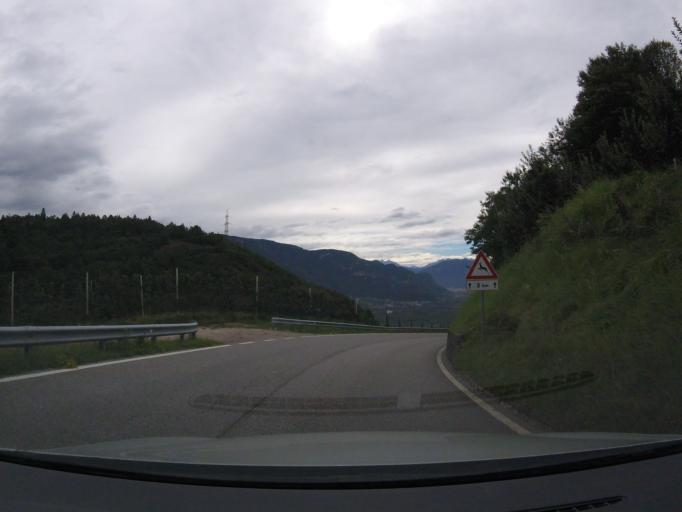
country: IT
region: Trentino-Alto Adige
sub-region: Bolzano
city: Tesimo
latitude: 46.5523
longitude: 11.1841
